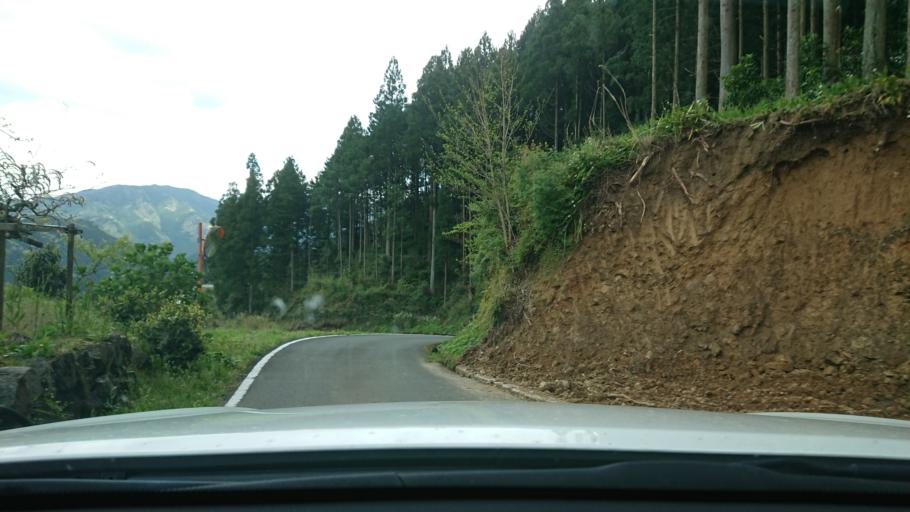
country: JP
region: Tokushima
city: Kamojimacho-jogejima
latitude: 33.8855
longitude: 134.3900
